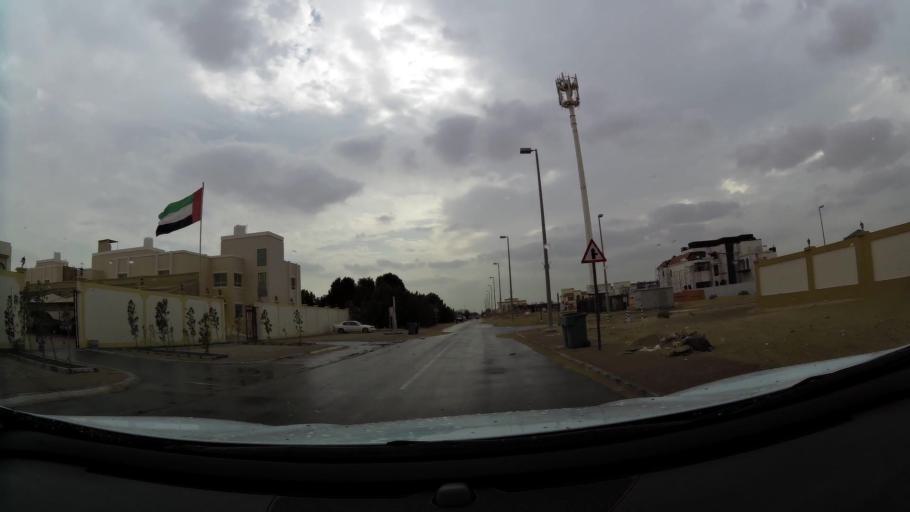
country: AE
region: Abu Dhabi
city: Abu Dhabi
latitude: 24.3650
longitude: 54.6254
